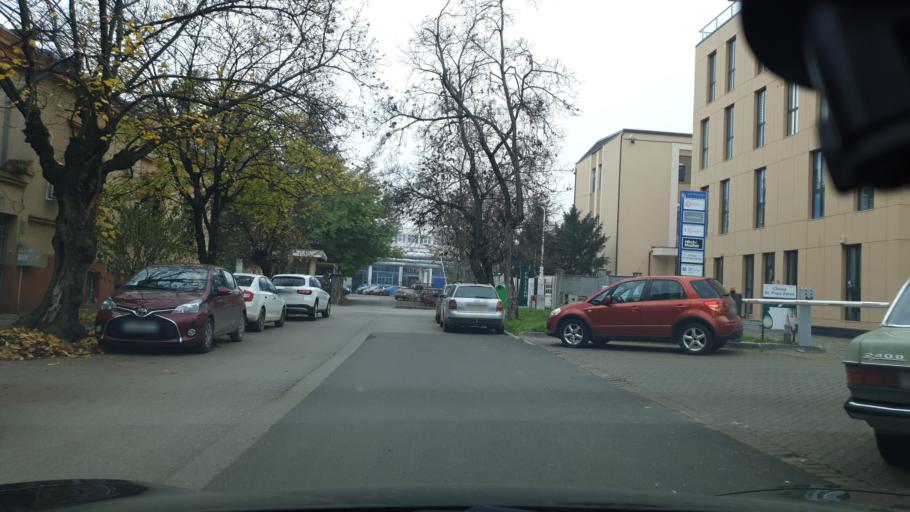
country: RO
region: Timis
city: Timisoara
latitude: 45.7562
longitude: 21.2451
